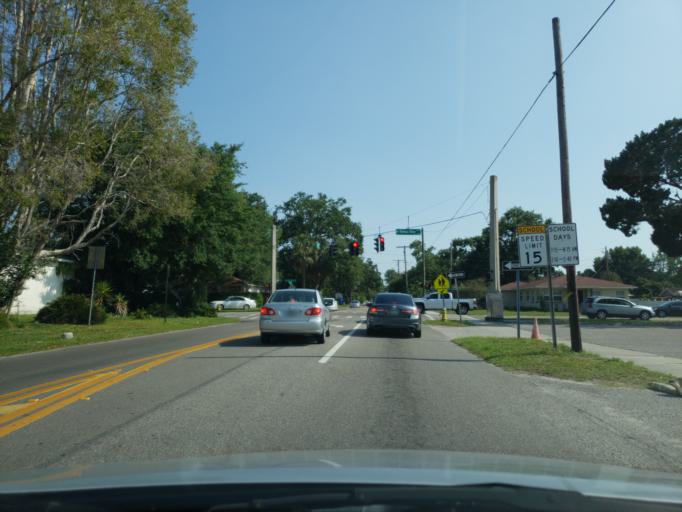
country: US
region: Florida
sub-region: Hillsborough County
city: Tampa
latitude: 27.9745
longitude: -82.4931
